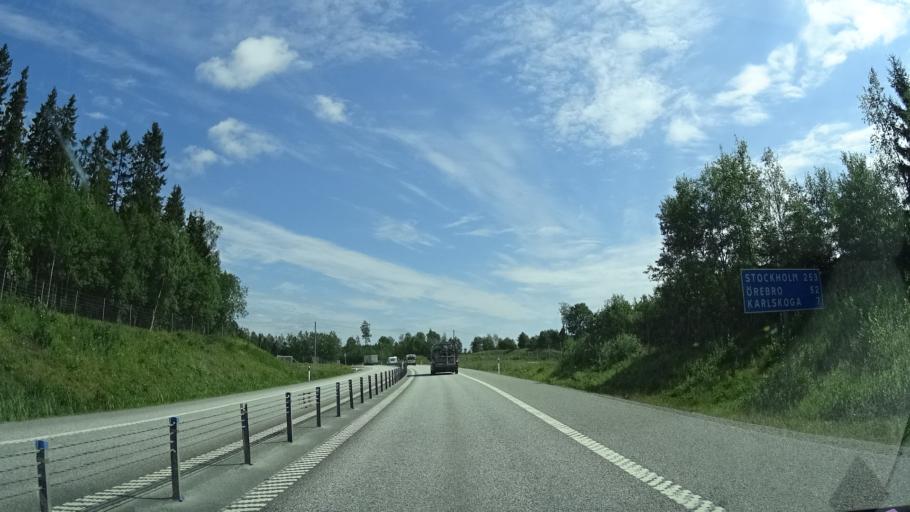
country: SE
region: OErebro
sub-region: Degerfors Kommun
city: Degerfors
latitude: 59.3213
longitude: 14.4085
